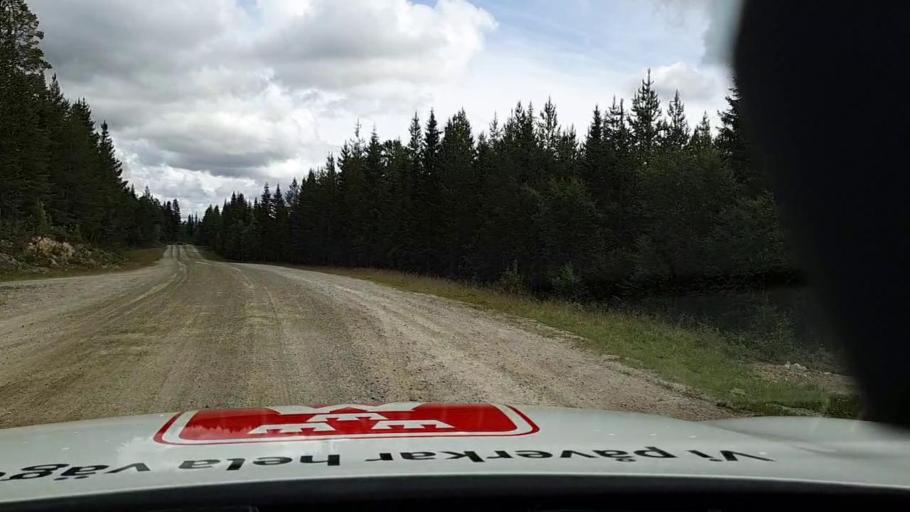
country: SE
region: Jaemtland
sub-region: Are Kommun
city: Jarpen
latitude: 62.5788
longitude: 13.3901
